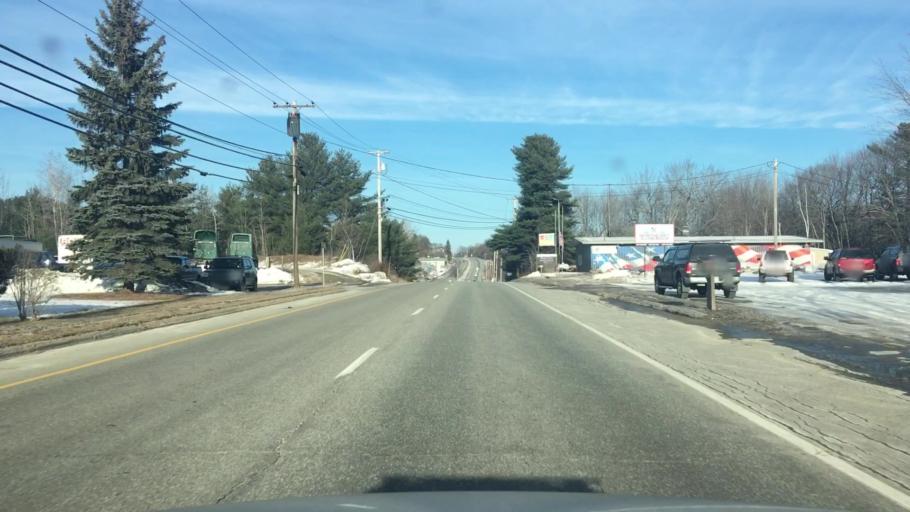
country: US
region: Maine
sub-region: Androscoggin County
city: Auburn
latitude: 44.0760
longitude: -70.2398
